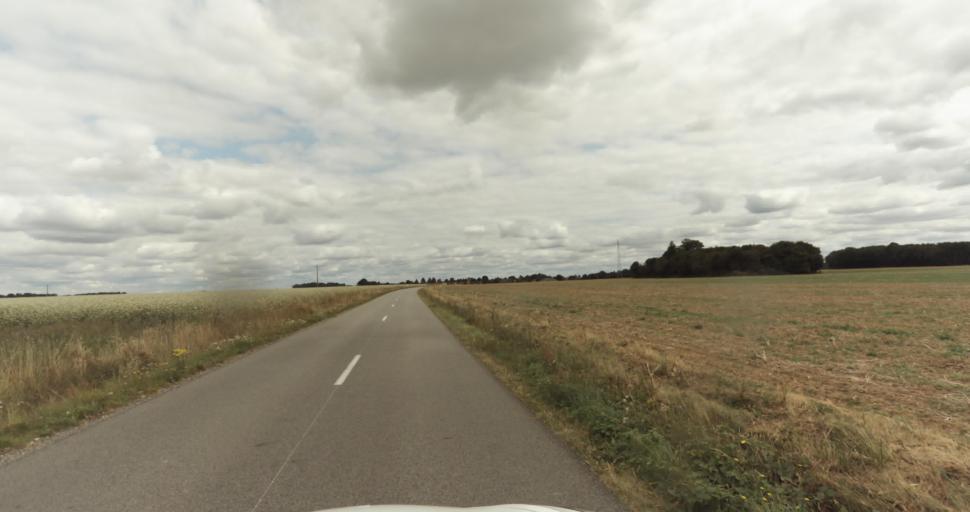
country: FR
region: Haute-Normandie
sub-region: Departement de l'Eure
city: Saint-Germain-sur-Avre
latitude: 48.7988
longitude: 1.2519
